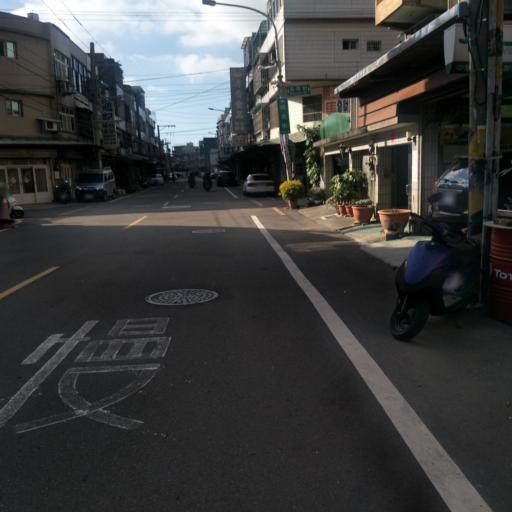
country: TW
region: Taiwan
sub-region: Hsinchu
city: Hsinchu
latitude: 24.7935
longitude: 120.9255
